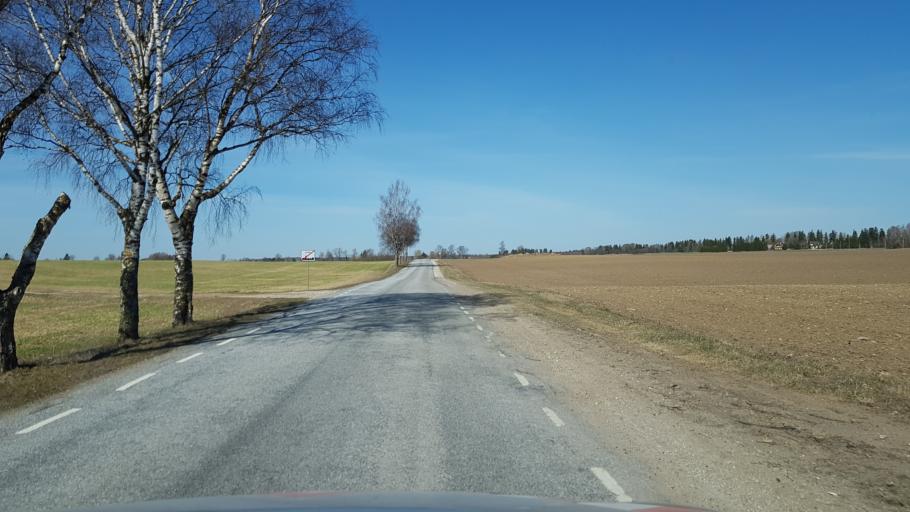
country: EE
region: Laeaene-Virumaa
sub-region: Vinni vald
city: Vinni
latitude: 59.2973
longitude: 26.4208
